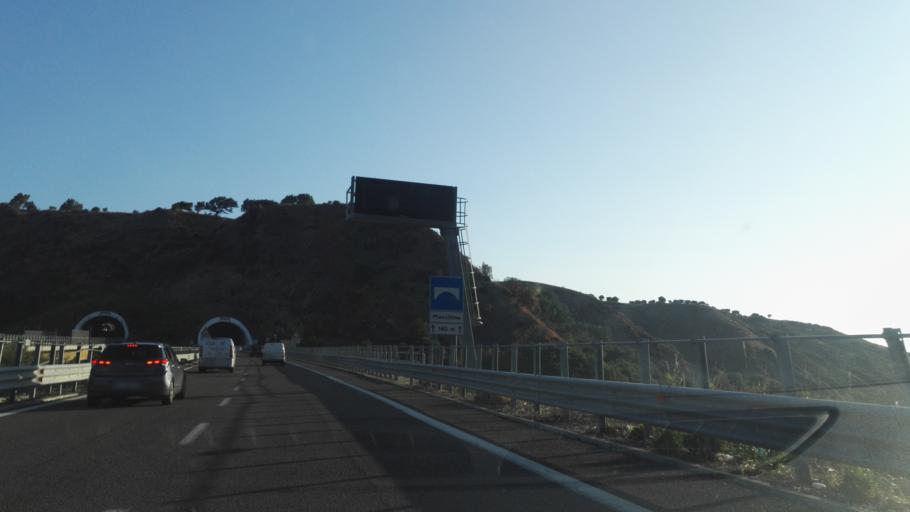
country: IT
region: Calabria
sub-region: Provincia di Catanzaro
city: Squillace Lido
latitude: 38.8032
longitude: 16.5556
